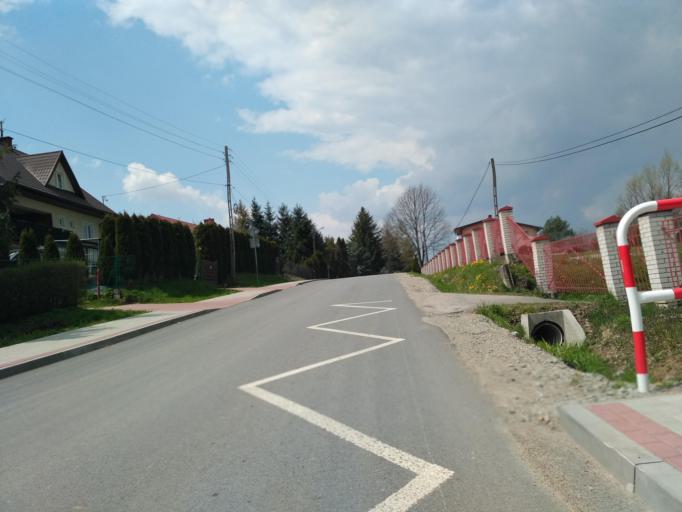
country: PL
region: Subcarpathian Voivodeship
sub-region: Powiat sanocki
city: Strachocina
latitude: 49.5874
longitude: 22.1130
